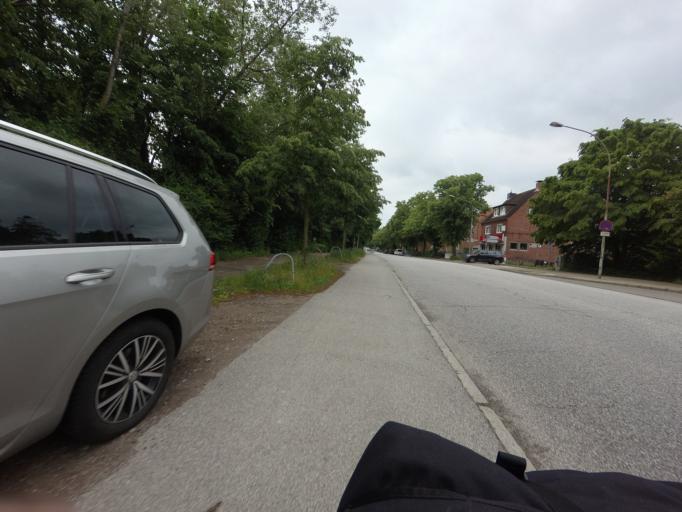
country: DE
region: Mecklenburg-Vorpommern
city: Selmsdorf
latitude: 53.9079
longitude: 10.8037
